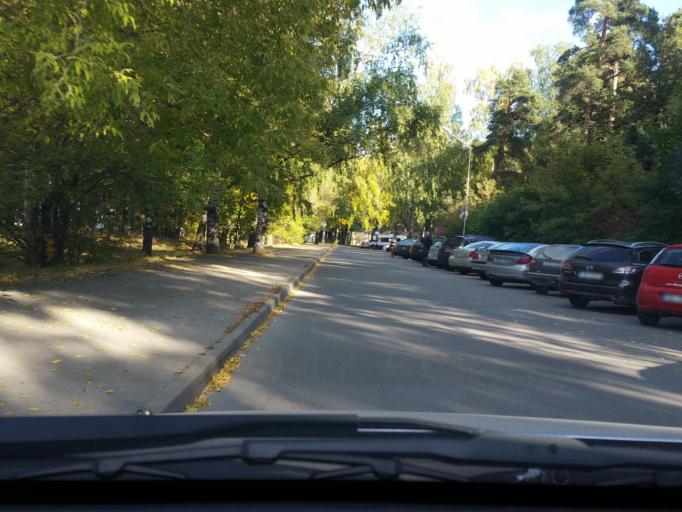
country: LV
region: Riga
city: Jaunciems
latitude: 56.9757
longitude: 24.1960
